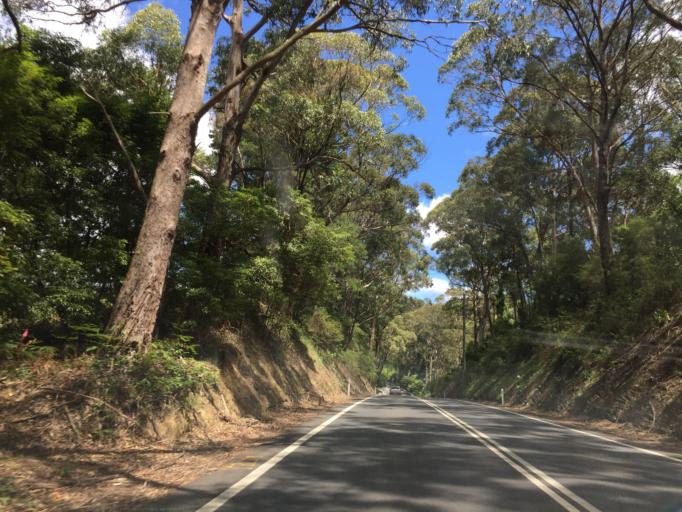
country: AU
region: New South Wales
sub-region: Blue Mountains Municipality
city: Lawson
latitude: -33.5302
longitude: 150.4502
